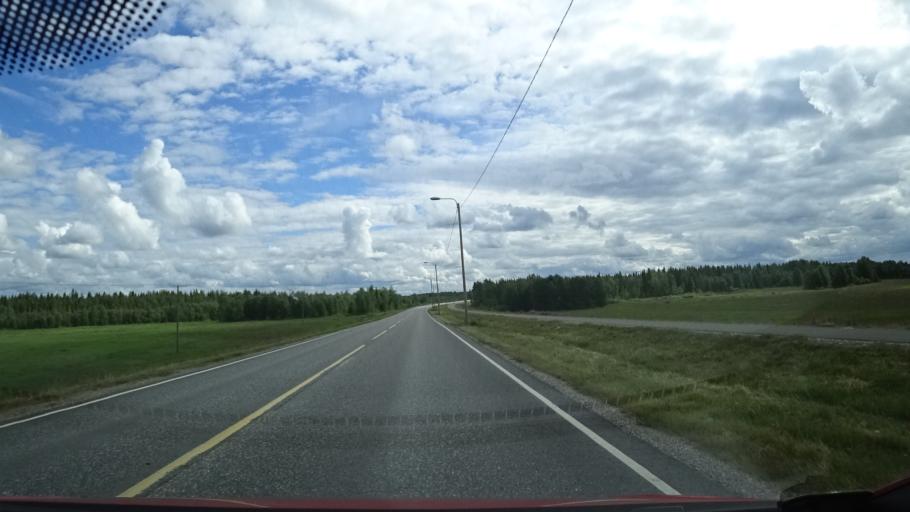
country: FI
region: Lapland
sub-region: Tunturi-Lappi
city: Kittilae
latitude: 67.4847
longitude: 24.9161
